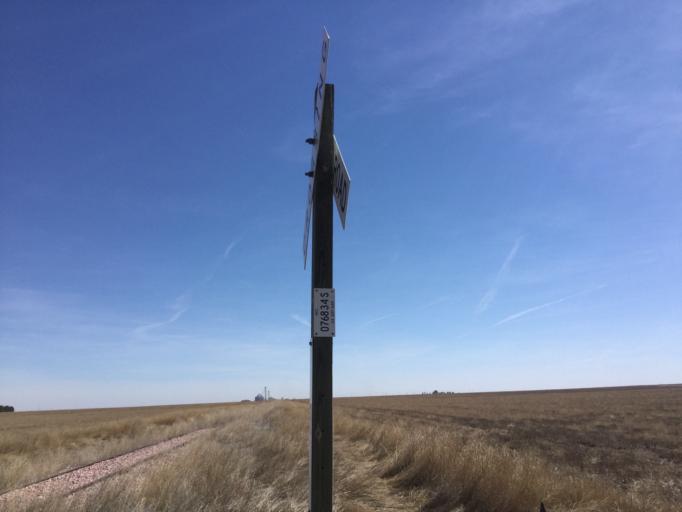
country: US
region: Kansas
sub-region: Cheyenne County
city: Saint Francis
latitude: 39.7621
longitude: -101.6174
